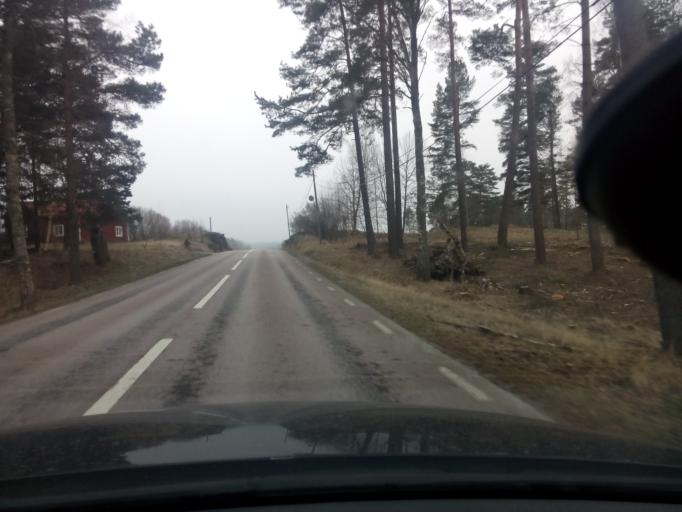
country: SE
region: Soedermanland
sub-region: Gnesta Kommun
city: Gnesta
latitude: 58.9495
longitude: 17.1250
